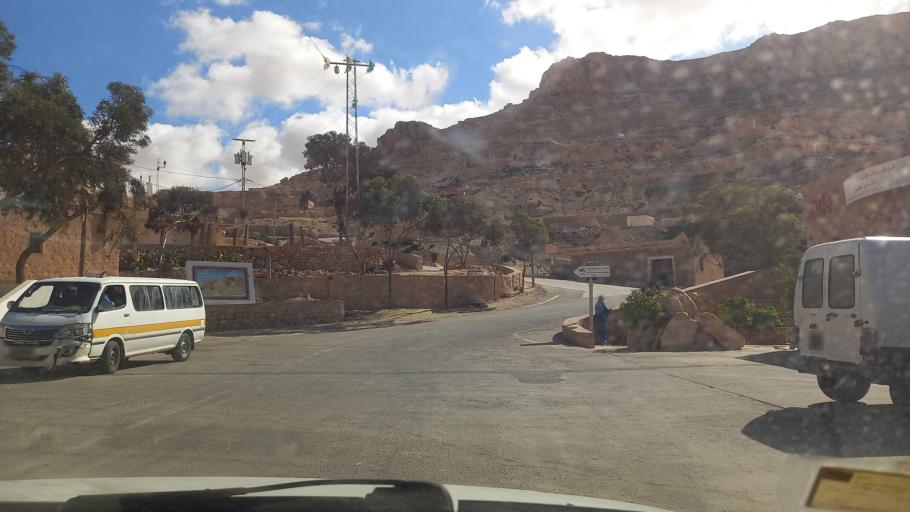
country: TN
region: Tataouine
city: Tataouine
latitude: 32.9107
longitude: 10.2608
